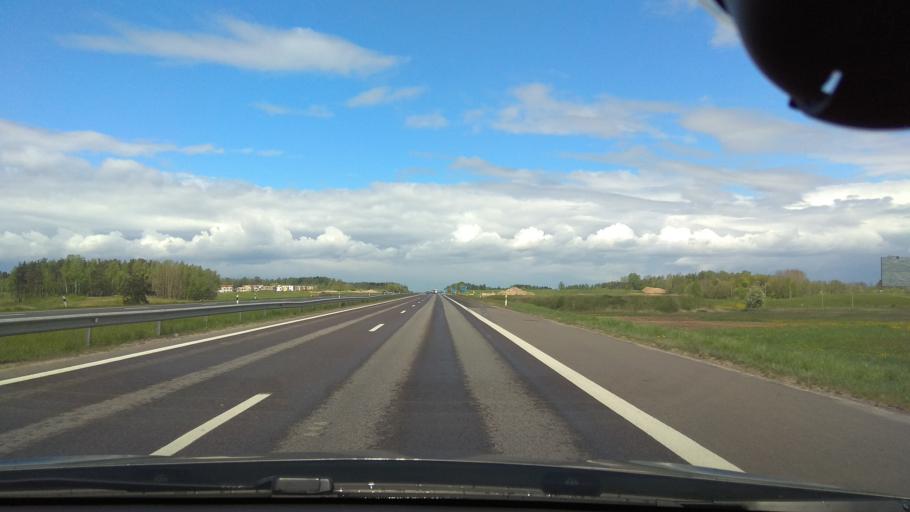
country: LT
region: Vilnius County
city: Pasilaiciai
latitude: 54.7803
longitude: 25.1835
